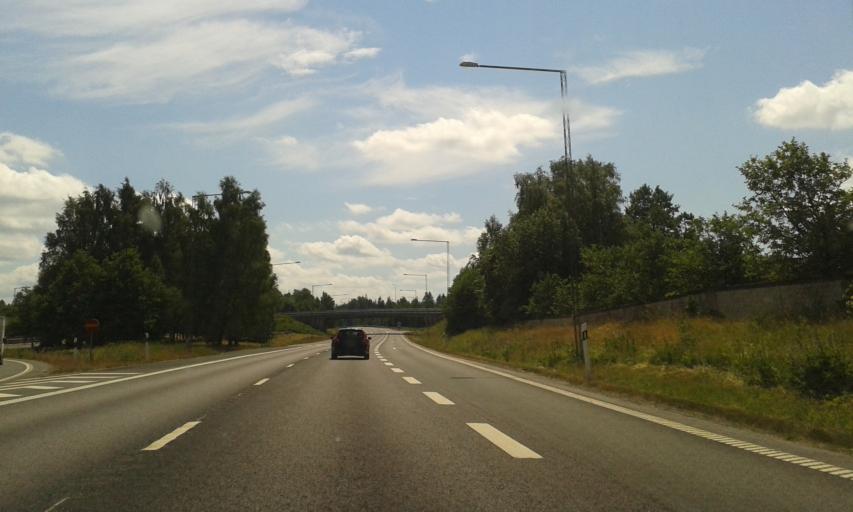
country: SE
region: Joenkoeping
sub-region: Varnamo Kommun
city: Rydaholm
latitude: 56.9878
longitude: 14.2990
